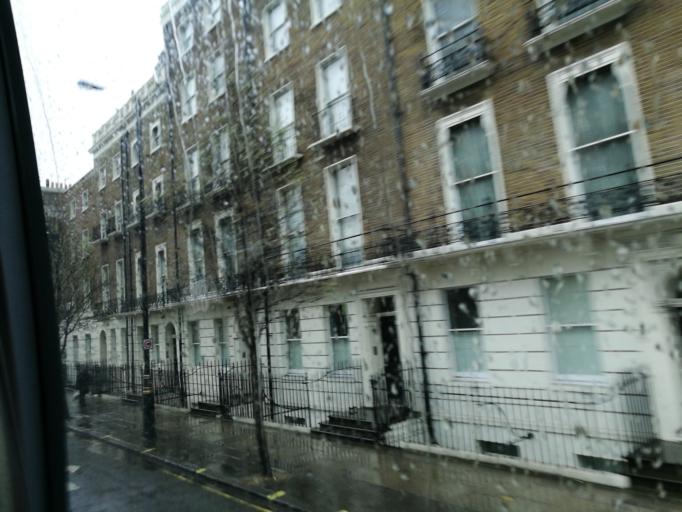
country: GB
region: England
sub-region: Greater London
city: Camden Town
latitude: 51.5166
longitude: -0.1571
